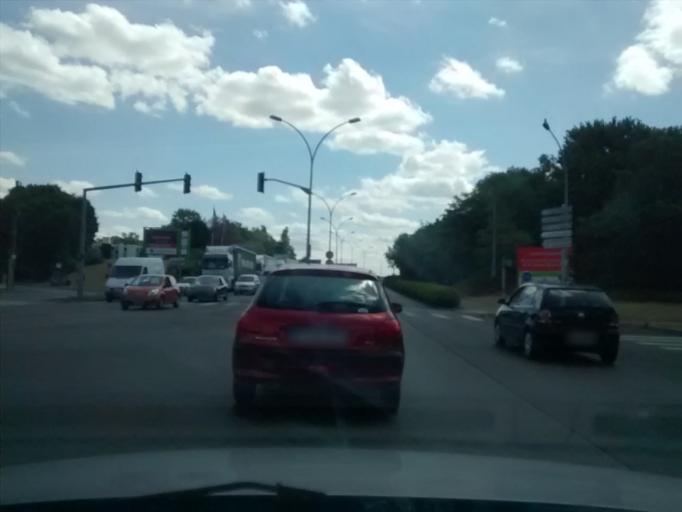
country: FR
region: Pays de la Loire
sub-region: Departement de la Sarthe
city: Le Mans
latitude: 47.9843
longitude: 0.1853
